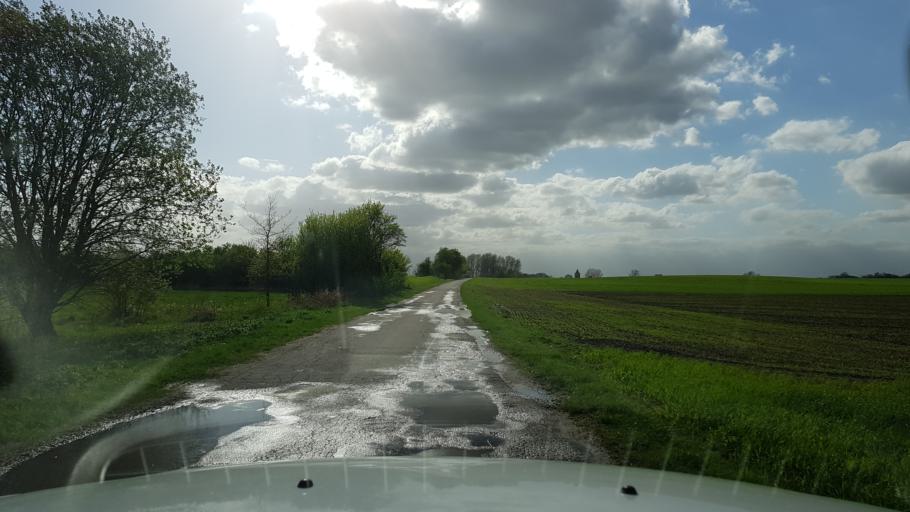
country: PL
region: West Pomeranian Voivodeship
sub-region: Powiat pyrzycki
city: Przelewice
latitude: 53.0222
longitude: 15.0942
